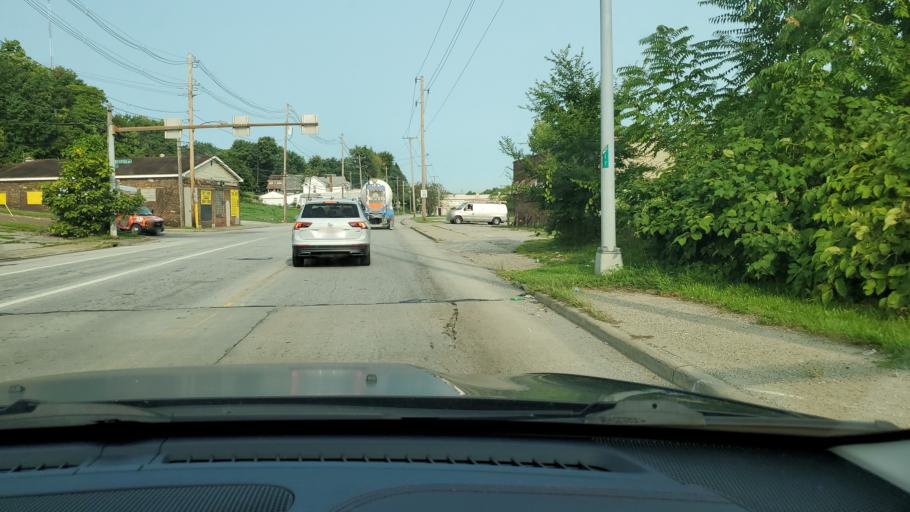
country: US
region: Ohio
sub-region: Mahoning County
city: Campbell
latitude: 41.0771
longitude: -80.6246
